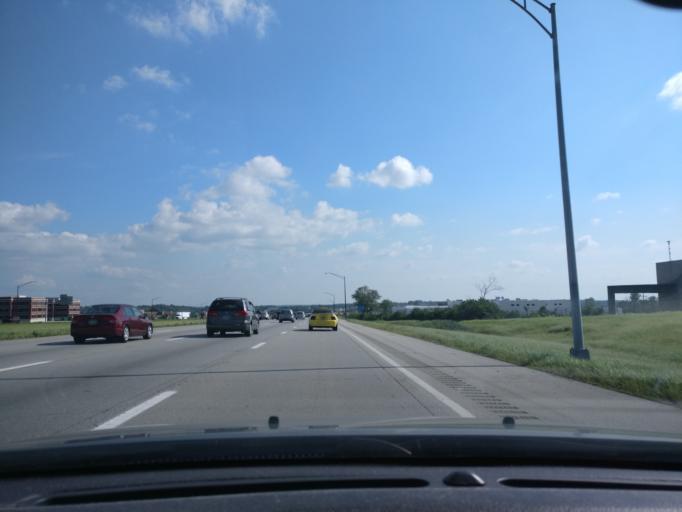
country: US
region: Ohio
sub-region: Warren County
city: Springboro
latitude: 39.6045
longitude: -84.2362
